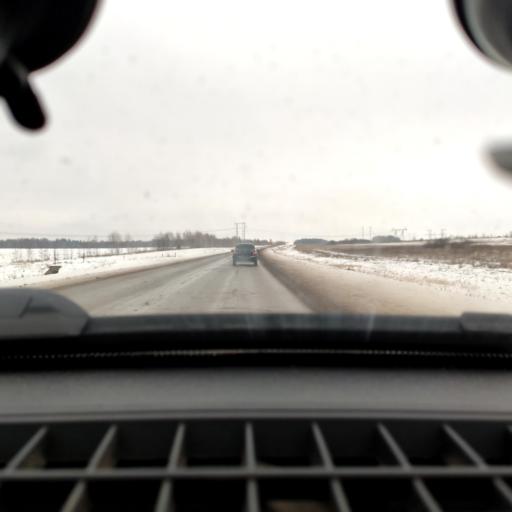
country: RU
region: Bashkortostan
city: Iglino
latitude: 54.7865
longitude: 56.4182
